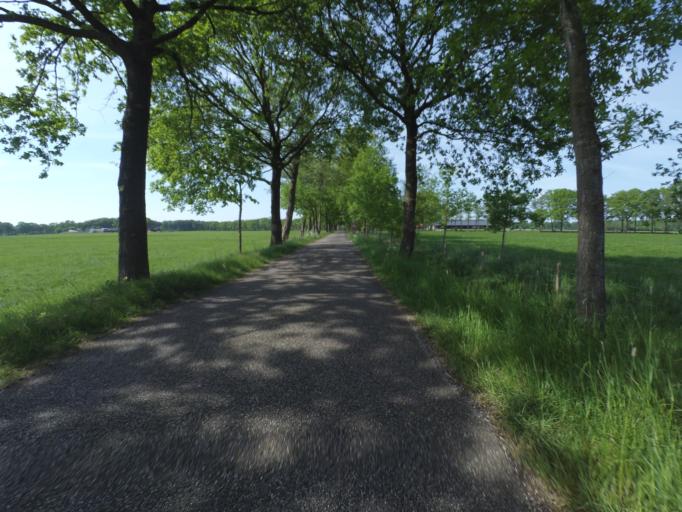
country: NL
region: Overijssel
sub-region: Gemeente Almelo
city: Almelo
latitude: 52.3529
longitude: 6.7033
